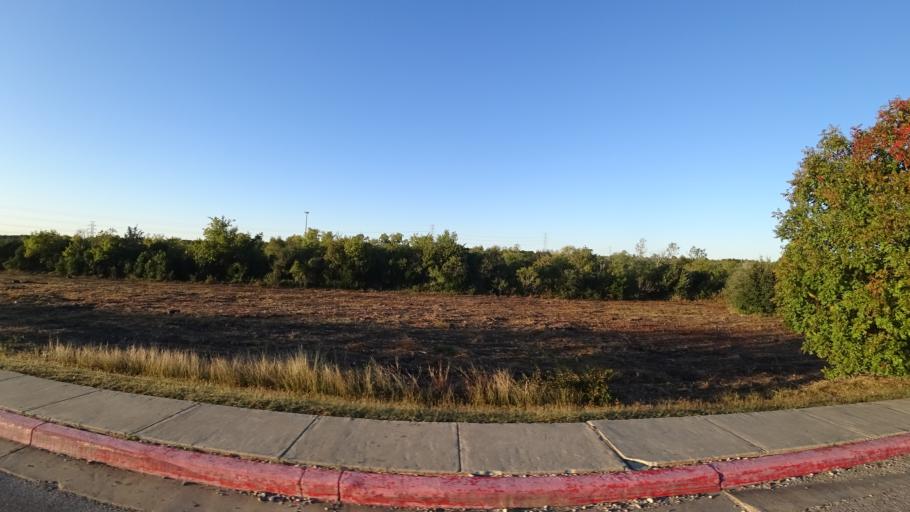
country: US
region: Texas
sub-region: Travis County
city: Hornsby Bend
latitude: 30.3059
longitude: -97.6207
